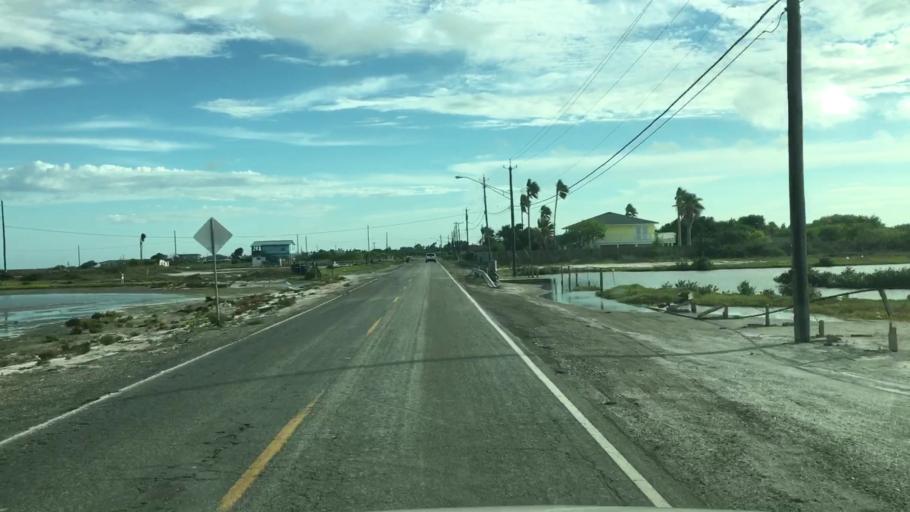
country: US
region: Texas
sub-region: Nueces County
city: Corpus Christi
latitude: 27.6426
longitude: -97.2853
